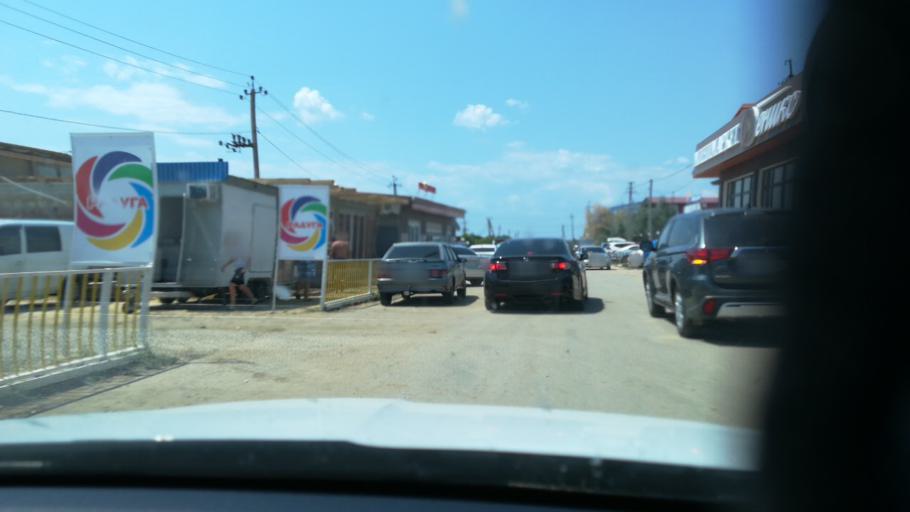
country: RU
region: Krasnodarskiy
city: Vyshestebliyevskaya
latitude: 45.1128
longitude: 36.8796
